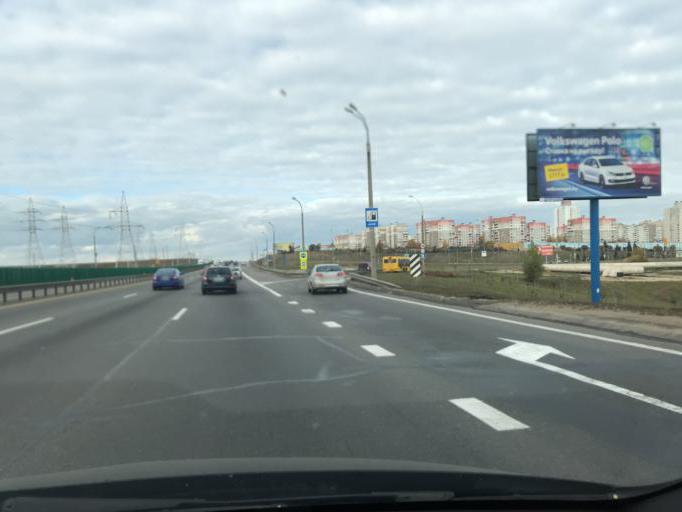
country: BY
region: Minsk
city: Malinovka
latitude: 53.8761
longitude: 27.4196
